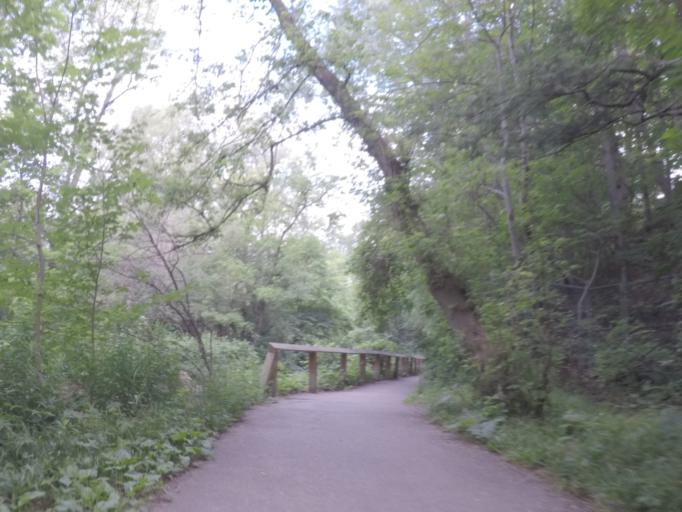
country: CA
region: Ontario
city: Etobicoke
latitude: 43.6545
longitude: -79.5474
